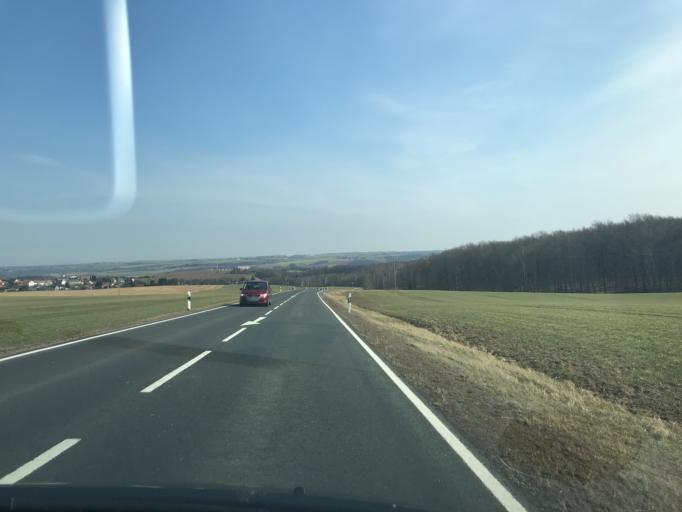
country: DE
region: Saxony
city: Wechselburg
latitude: 51.0316
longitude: 12.7583
